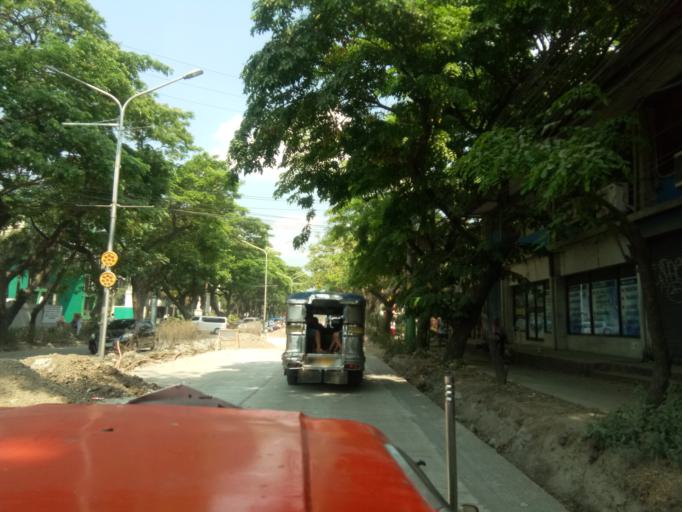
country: PH
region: Calabarzon
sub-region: Province of Cavite
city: Dasmarinas
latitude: 14.3267
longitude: 120.9422
